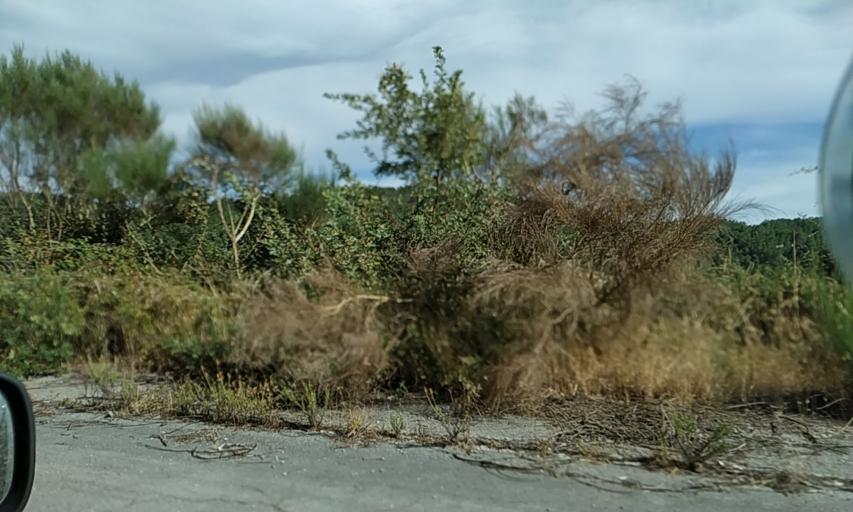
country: PT
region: Vila Real
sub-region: Sabrosa
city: Sabrosa
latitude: 41.3560
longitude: -7.5834
